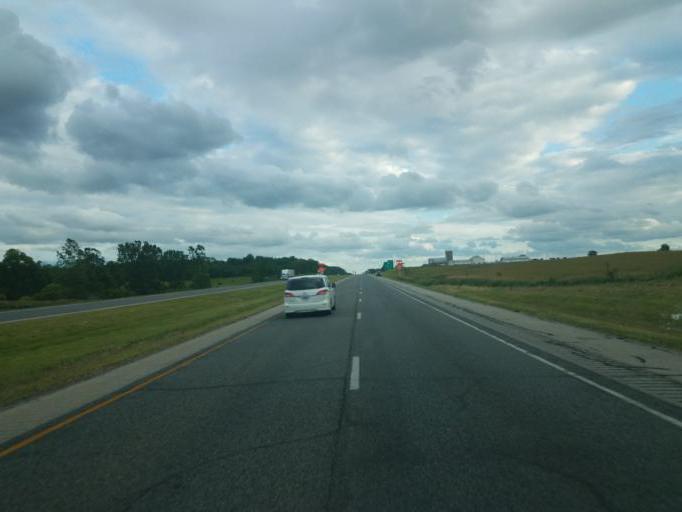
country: US
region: Indiana
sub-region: DeKalb County
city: Waterloo
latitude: 41.4609
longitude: -85.0543
